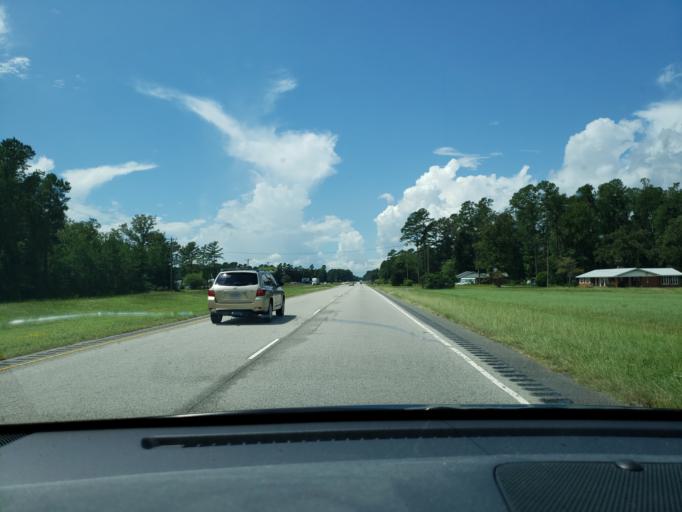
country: US
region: North Carolina
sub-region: Bladen County
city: Elizabethtown
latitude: 34.6455
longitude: -78.6910
